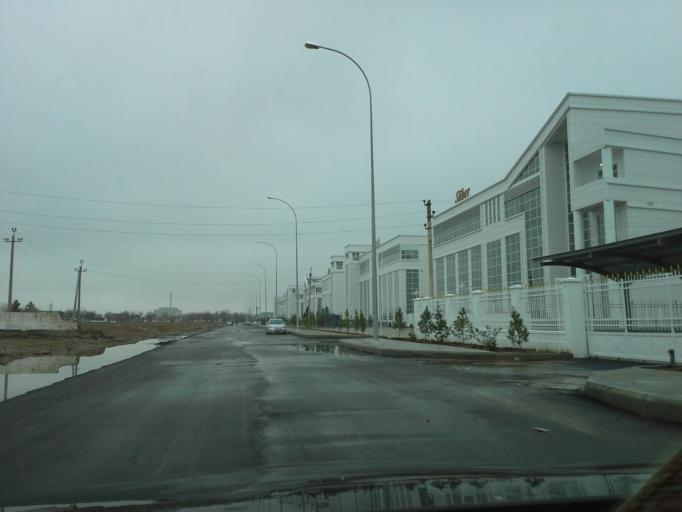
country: TM
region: Ahal
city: Ashgabat
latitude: 37.9505
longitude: 58.4312
